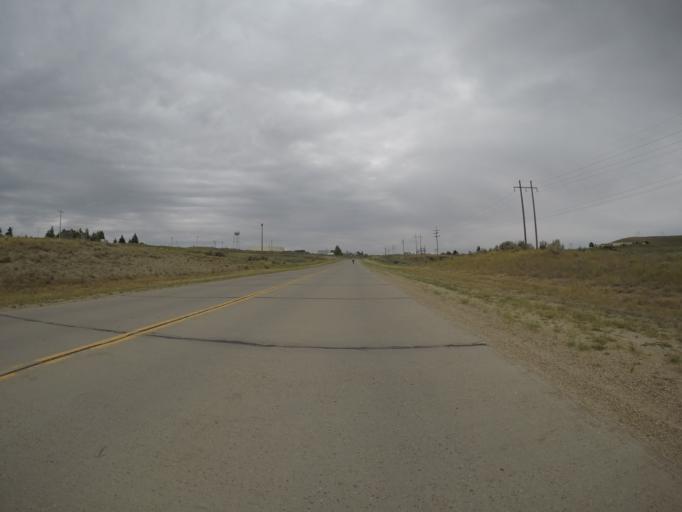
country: US
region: Wyoming
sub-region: Lincoln County
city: Kemmerer
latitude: 41.7950
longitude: -110.5476
